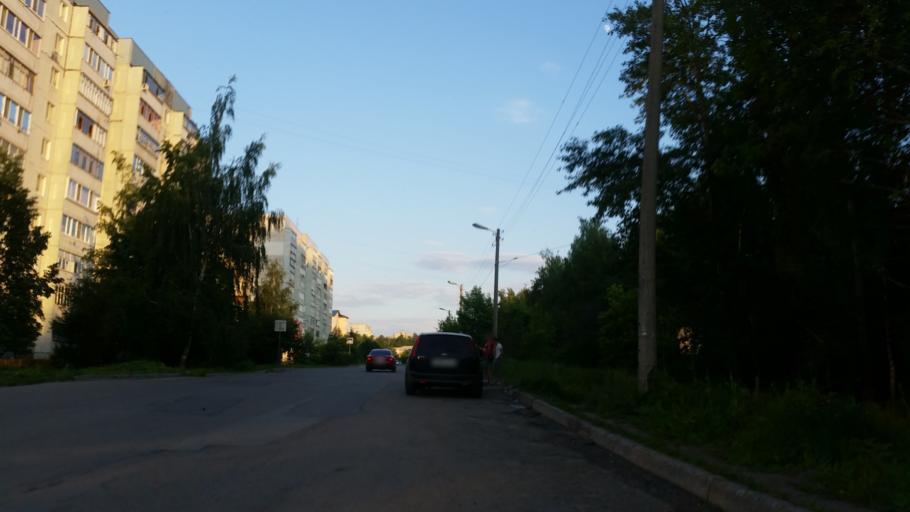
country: RU
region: Ulyanovsk
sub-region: Ulyanovskiy Rayon
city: Ulyanovsk
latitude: 54.3573
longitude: 48.3826
